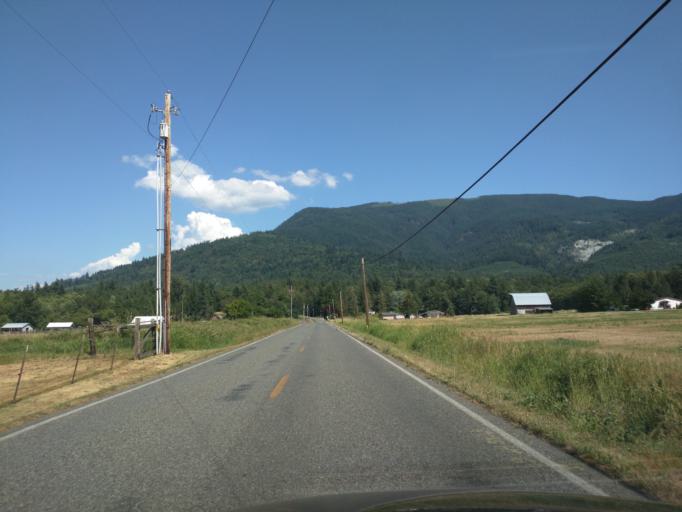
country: US
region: Washington
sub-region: Whatcom County
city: Nooksack
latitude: 48.9203
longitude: -122.2820
